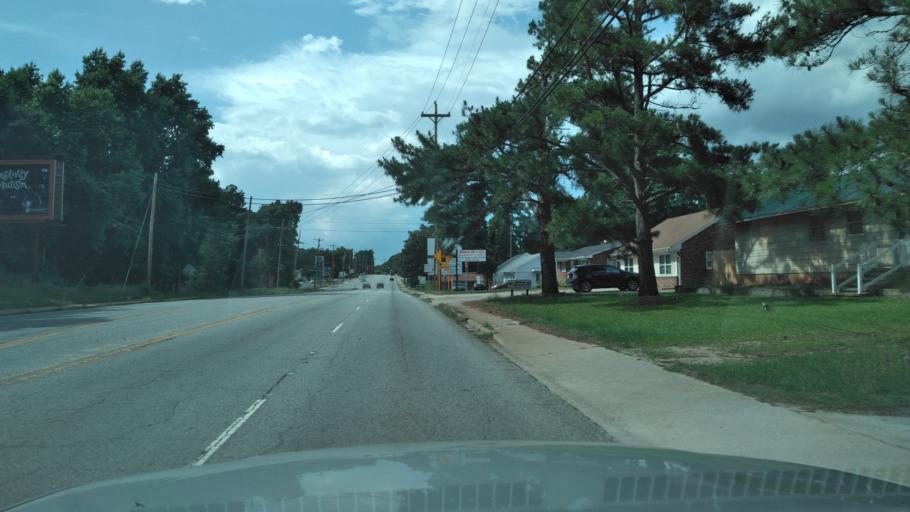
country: US
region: South Carolina
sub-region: Spartanburg County
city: Saxon
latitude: 34.9806
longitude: -81.9440
